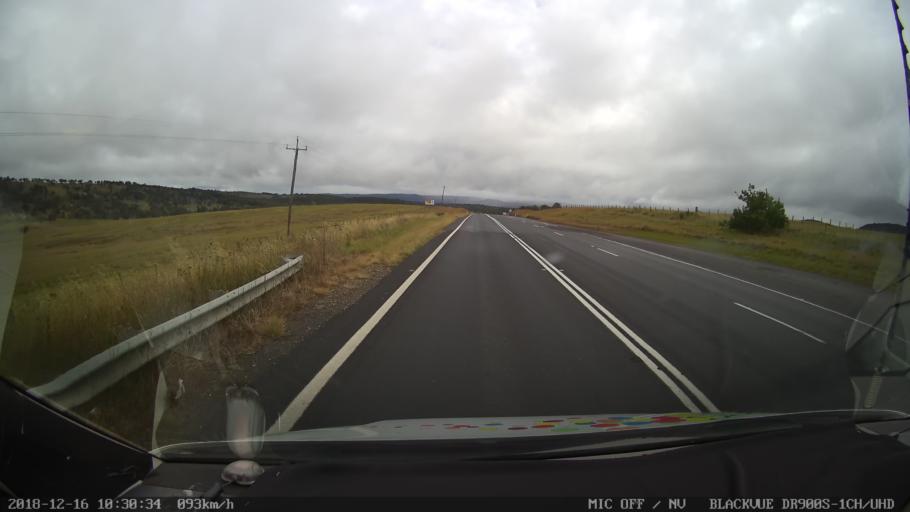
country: AU
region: New South Wales
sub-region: Tenterfield Municipality
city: Carrolls Creek
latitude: -29.0914
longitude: 152.0029
